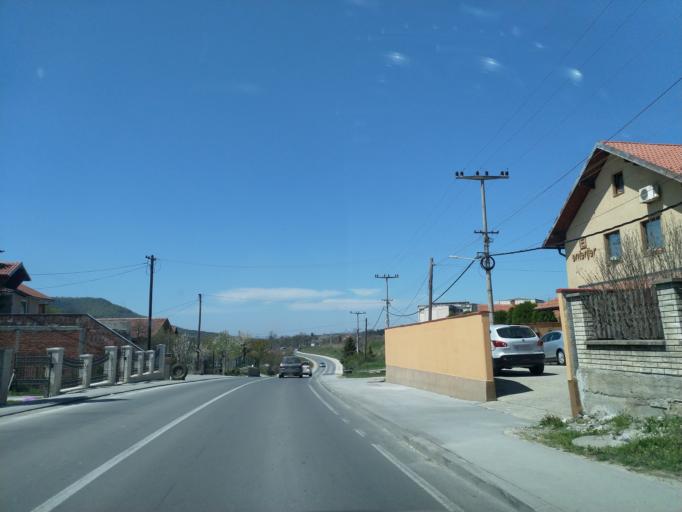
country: RS
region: Central Serbia
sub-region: Sumadijski Okrug
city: Arangelovac
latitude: 44.3253
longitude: 20.5287
